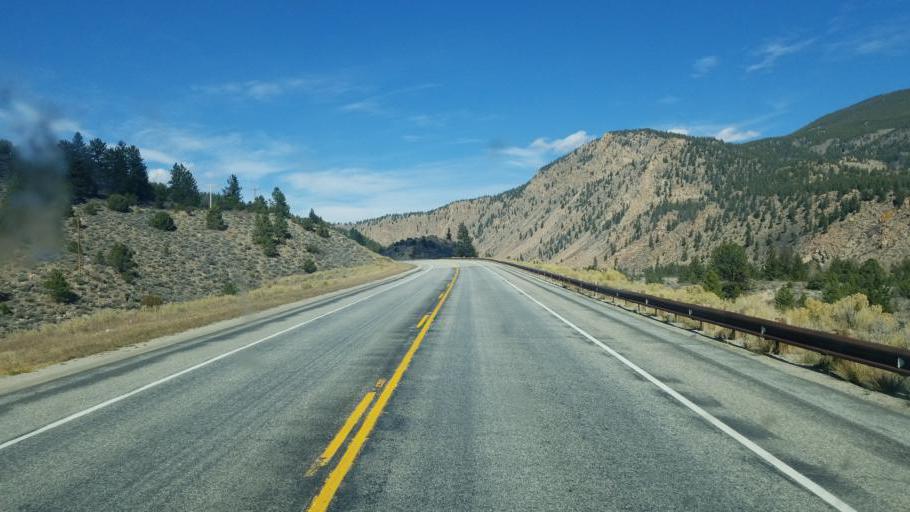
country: US
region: Colorado
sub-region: Chaffee County
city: Buena Vista
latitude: 38.9802
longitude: -106.2160
